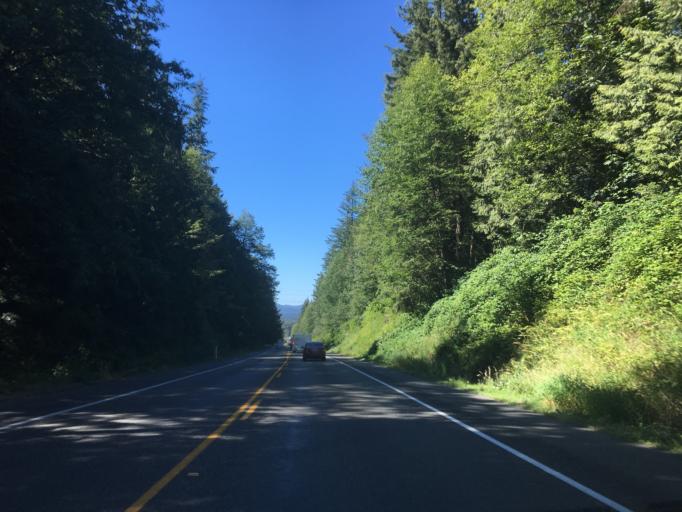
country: US
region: Washington
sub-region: Snohomish County
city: Arlington
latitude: 48.1686
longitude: -122.1210
